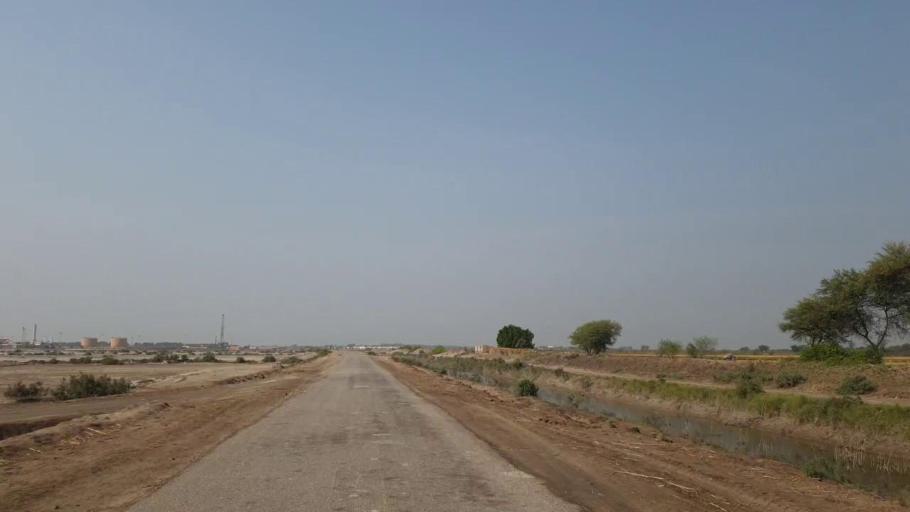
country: PK
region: Sindh
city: Tando Muhammad Khan
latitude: 24.9638
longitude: 68.5158
